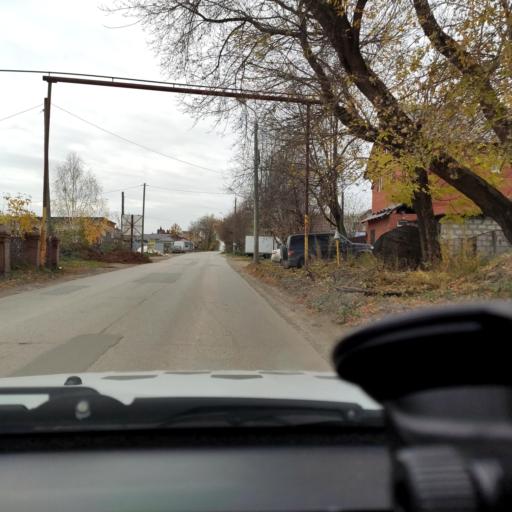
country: RU
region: Perm
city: Perm
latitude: 57.9963
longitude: 56.3133
